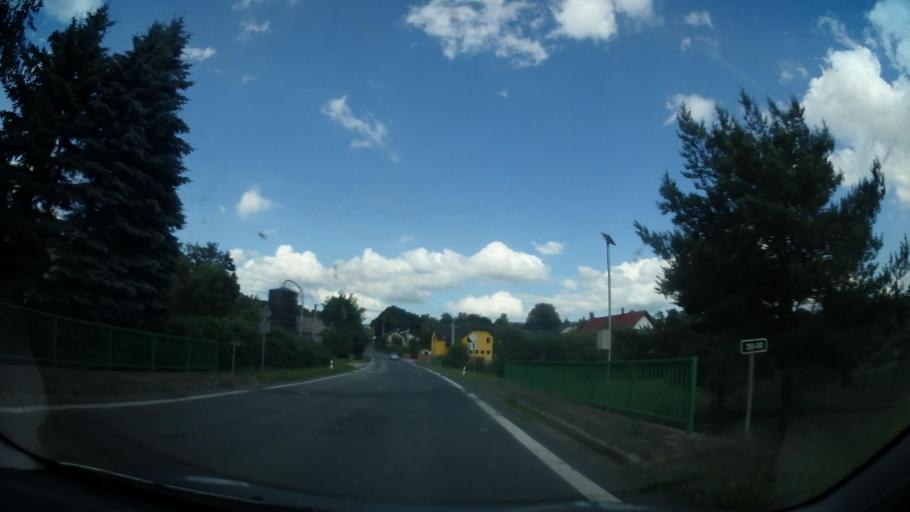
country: CZ
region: Vysocina
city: Zd'ar nad Sazavou Druhy
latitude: 49.6190
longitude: 15.9518
